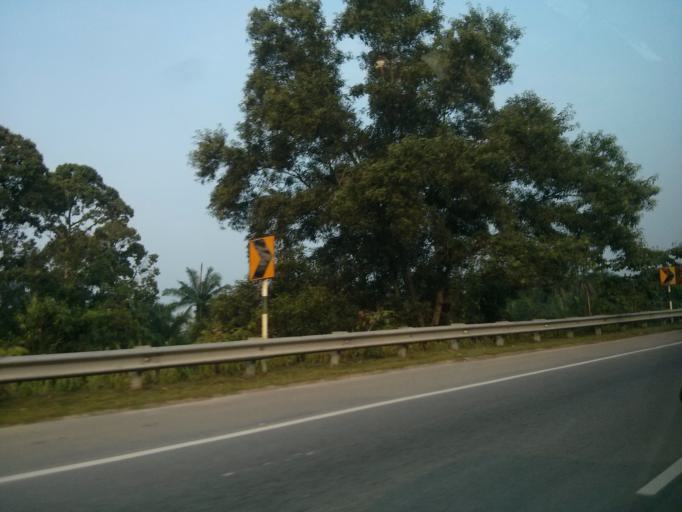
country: MY
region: Putrajaya
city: Putrajaya
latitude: 2.8627
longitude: 101.6884
